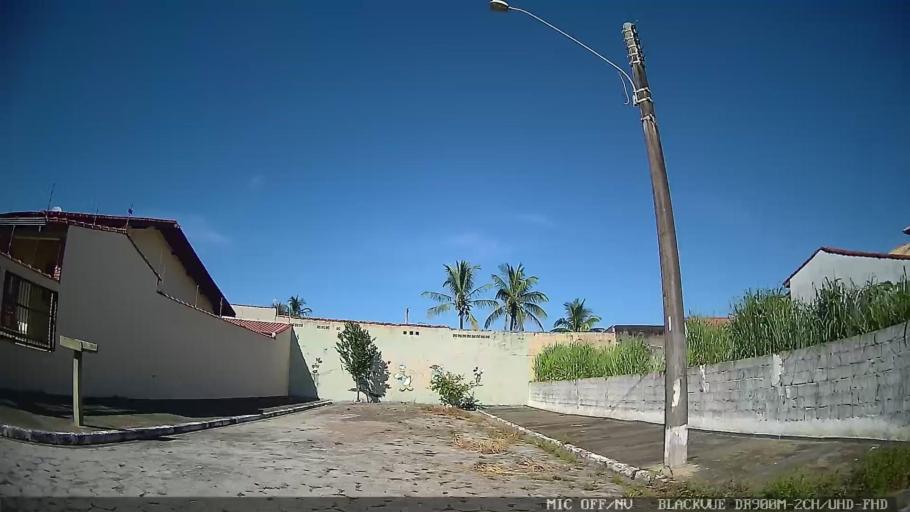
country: BR
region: Sao Paulo
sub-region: Peruibe
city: Peruibe
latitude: -24.2793
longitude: -46.9453
